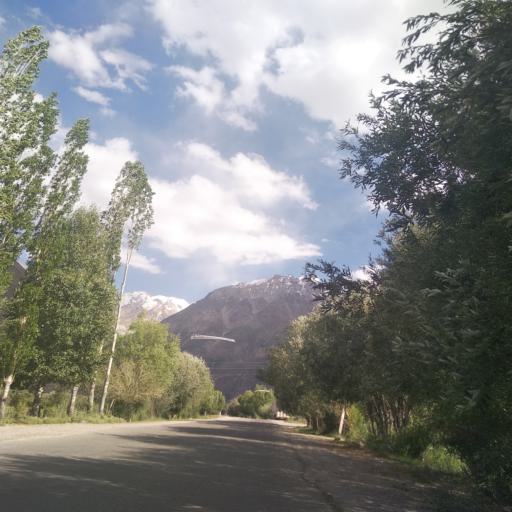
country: TJ
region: Gorno-Badakhshan
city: Roshtqal'a
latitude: 37.7249
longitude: 72.1612
